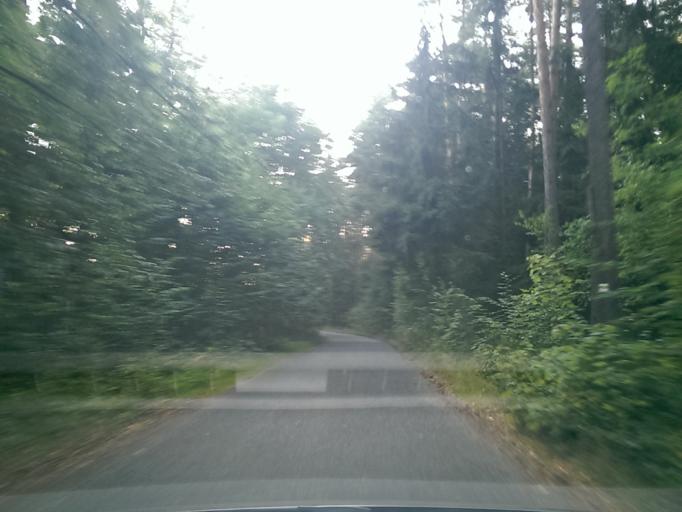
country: CZ
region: Central Bohemia
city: Bela pod Bezdezem
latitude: 50.4987
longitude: 14.7188
